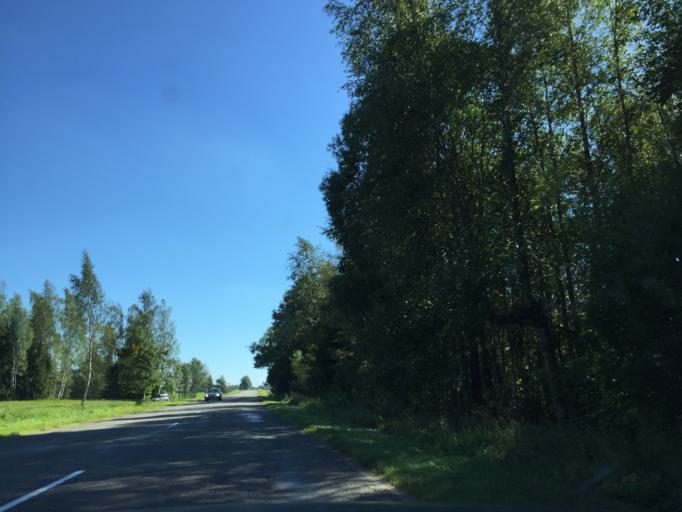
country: LV
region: Akniste
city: Akniste
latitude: 56.0704
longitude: 25.8904
